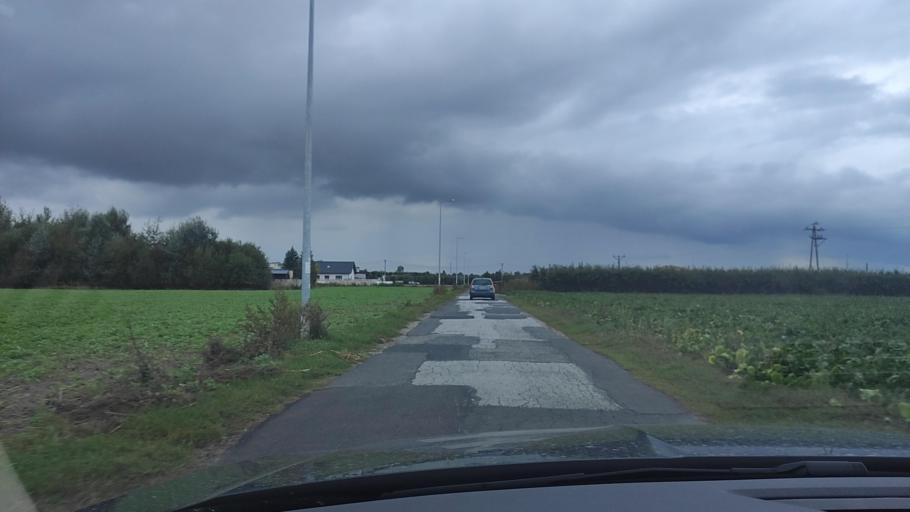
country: PL
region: Greater Poland Voivodeship
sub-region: Powiat poznanski
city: Kostrzyn
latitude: 52.3980
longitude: 17.1811
